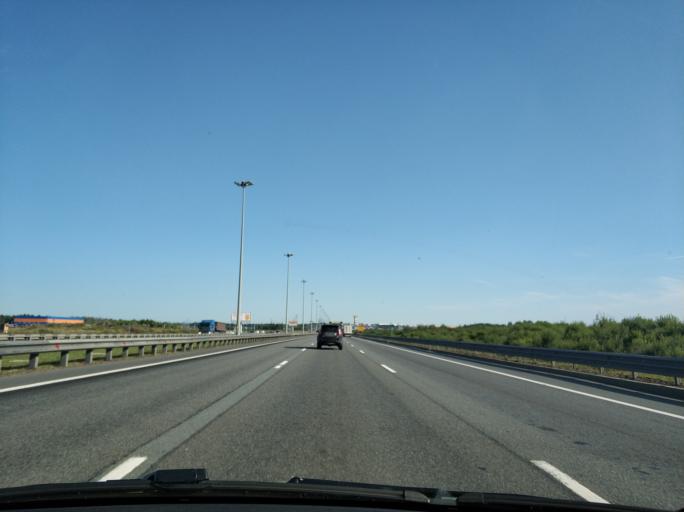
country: RU
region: Leningrad
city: Bugry
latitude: 60.0742
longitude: 30.3817
